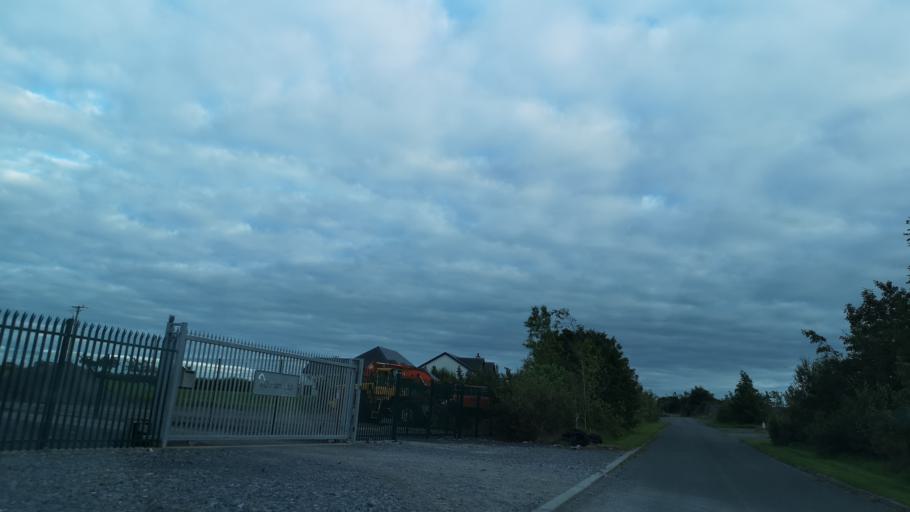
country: IE
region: Connaught
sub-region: County Galway
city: Athenry
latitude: 53.2864
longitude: -8.7552
